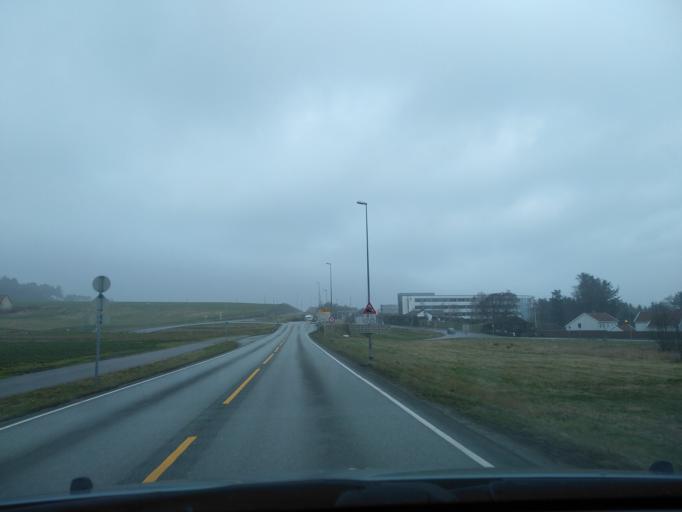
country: NO
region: Rogaland
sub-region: Randaberg
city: Randaberg
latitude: 59.0107
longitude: 5.6372
